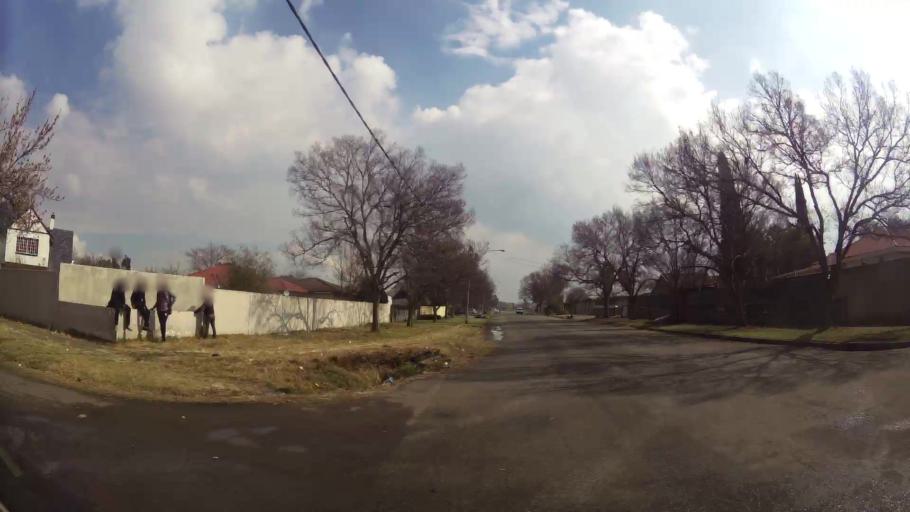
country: ZA
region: Gauteng
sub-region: Sedibeng District Municipality
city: Vereeniging
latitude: -26.6771
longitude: 27.9200
